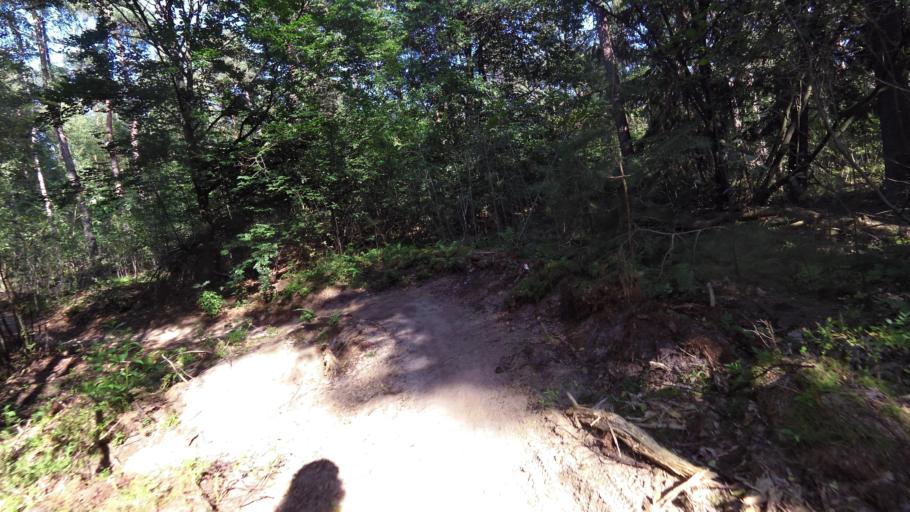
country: NL
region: Gelderland
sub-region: Gemeente Arnhem
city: Hoogkamp
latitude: 52.0126
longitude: 5.8829
